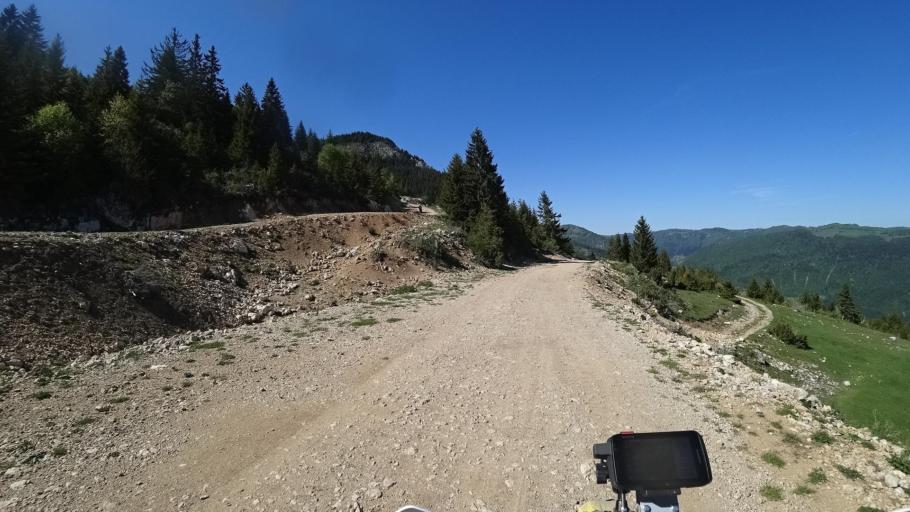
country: BA
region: Federation of Bosnia and Herzegovina
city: Travnik
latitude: 44.2858
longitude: 17.6937
